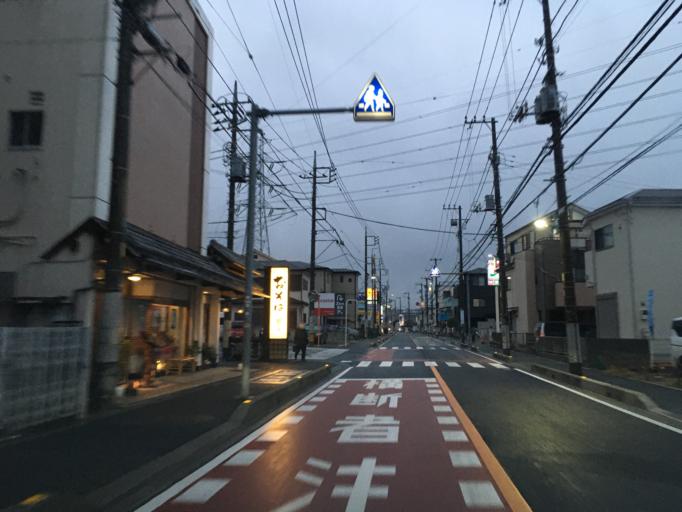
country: JP
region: Saitama
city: Asaka
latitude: 35.7881
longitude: 139.5954
